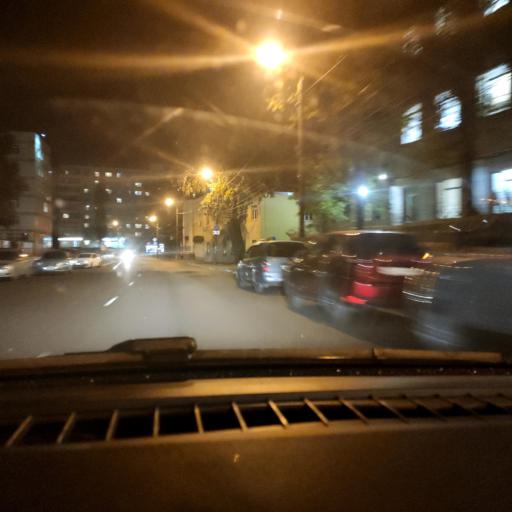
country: RU
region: Voronezj
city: Voronezh
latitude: 51.6754
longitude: 39.2503
